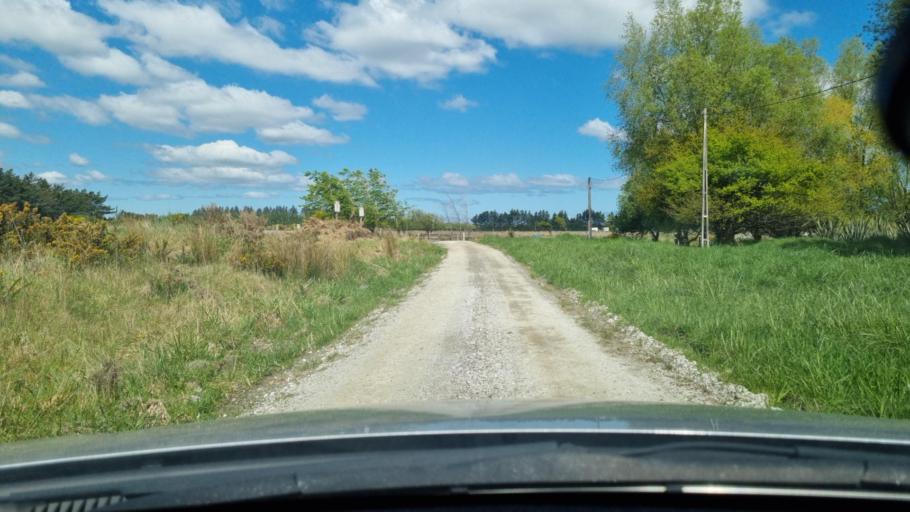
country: NZ
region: Southland
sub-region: Invercargill City
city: Invercargill
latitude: -46.3489
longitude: 168.3400
